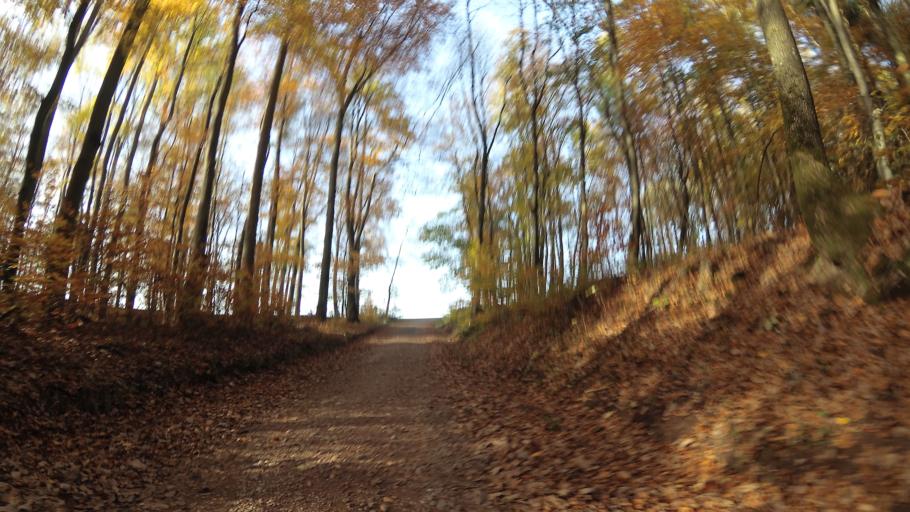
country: DE
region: Saarland
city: Hangard
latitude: 49.3739
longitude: 7.2287
